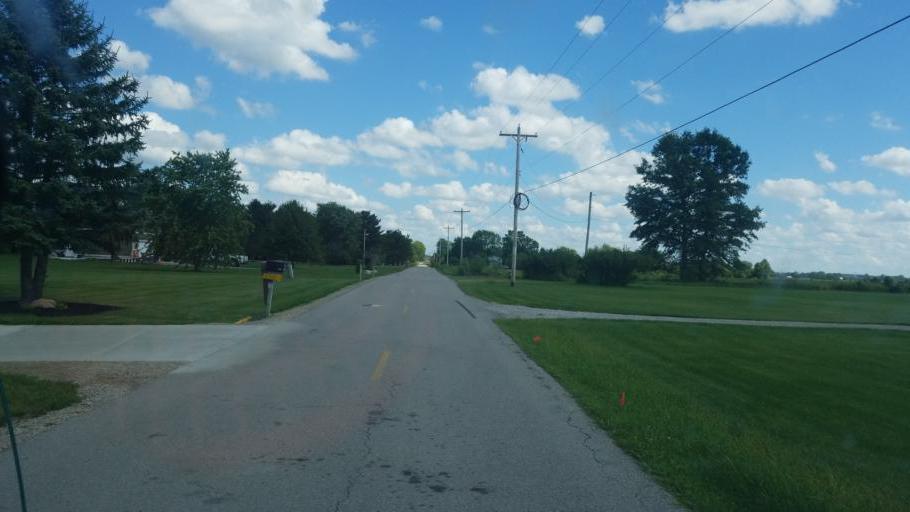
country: US
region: Ohio
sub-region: Union County
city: Richwood
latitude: 40.3139
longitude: -83.2153
